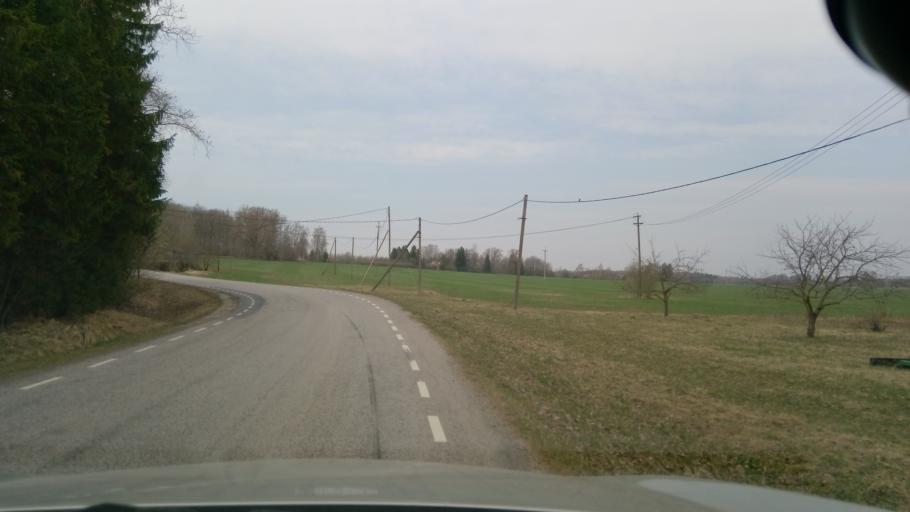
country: EE
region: Jaervamaa
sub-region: Tueri vald
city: Sarevere
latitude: 58.7830
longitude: 25.4784
